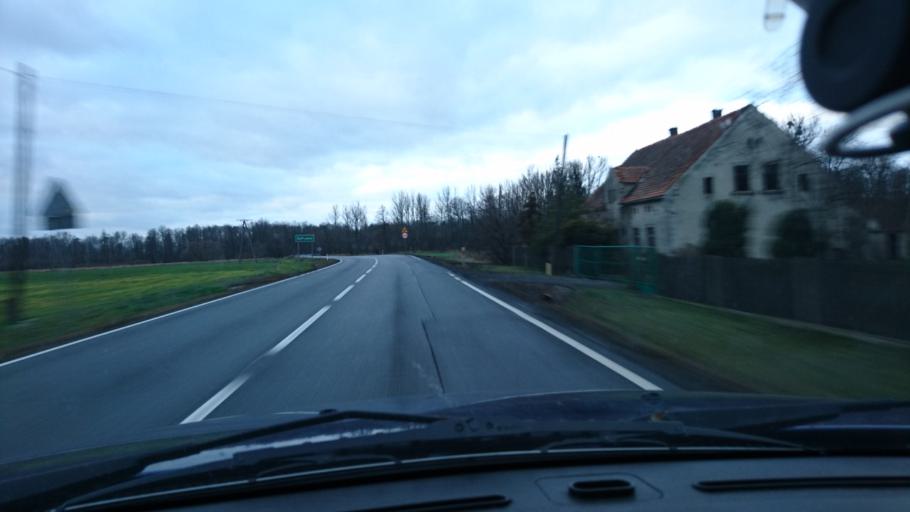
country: PL
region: Opole Voivodeship
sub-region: Powiat kluczborski
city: Byczyna
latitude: 51.1415
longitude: 18.1946
